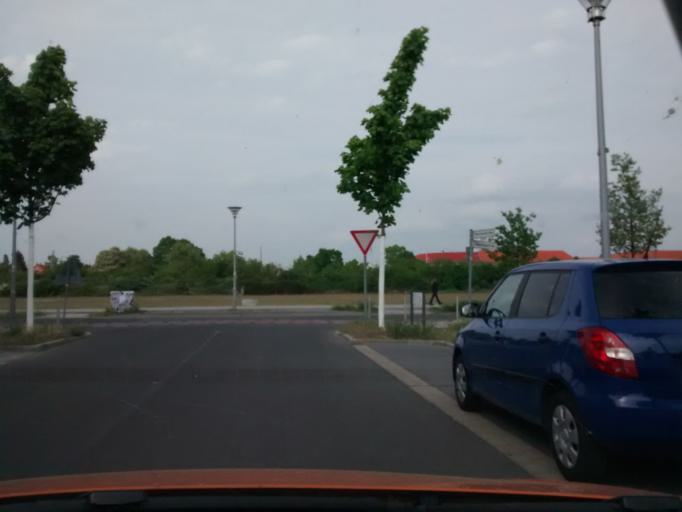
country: DE
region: Berlin
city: Adlershof
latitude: 52.4365
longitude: 13.5349
